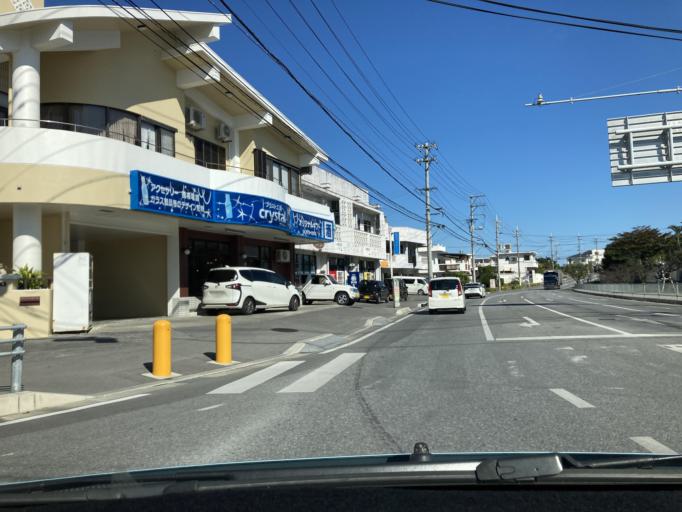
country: JP
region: Okinawa
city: Gushikawa
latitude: 26.3724
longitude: 127.8600
